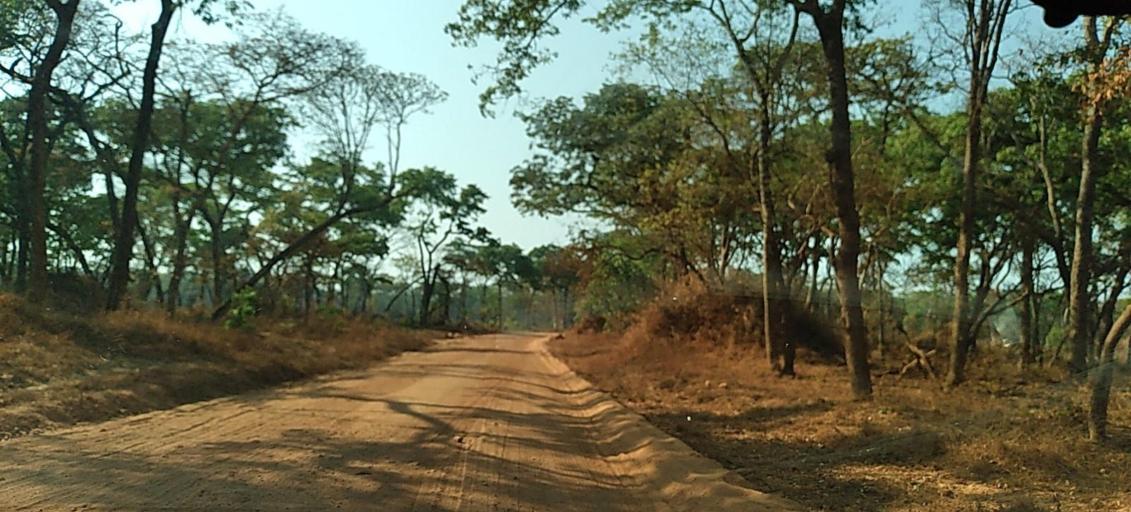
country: ZM
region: North-Western
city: Kasempa
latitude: -13.6718
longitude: 26.0169
